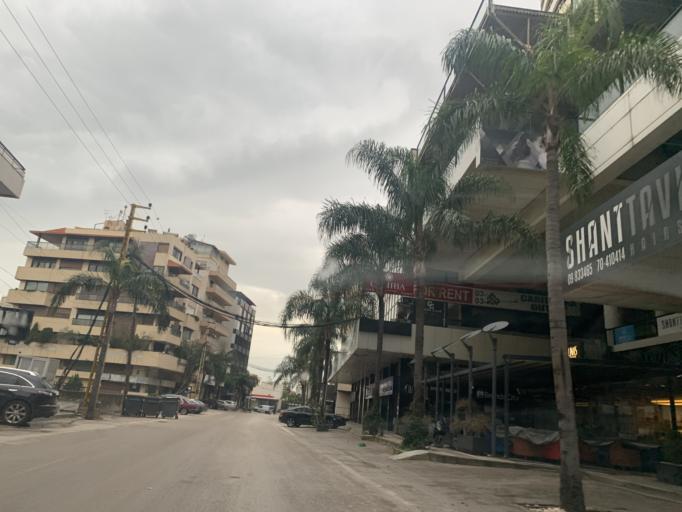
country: LB
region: Mont-Liban
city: Djounie
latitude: 33.9790
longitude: 35.6156
